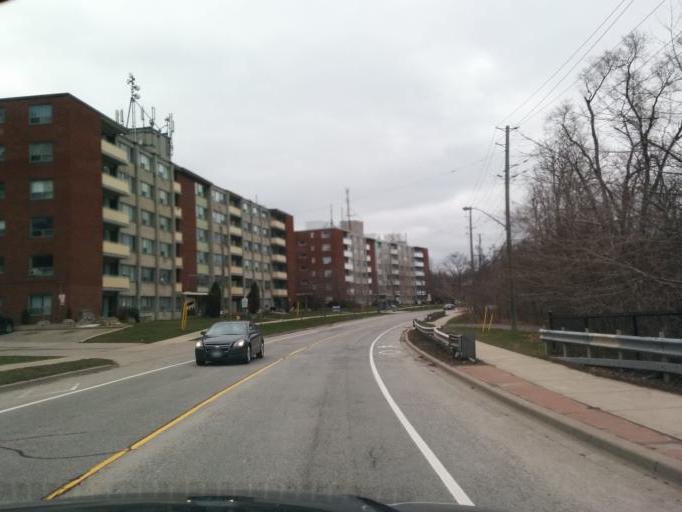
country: CA
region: Ontario
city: Etobicoke
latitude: 43.6383
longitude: -79.5080
